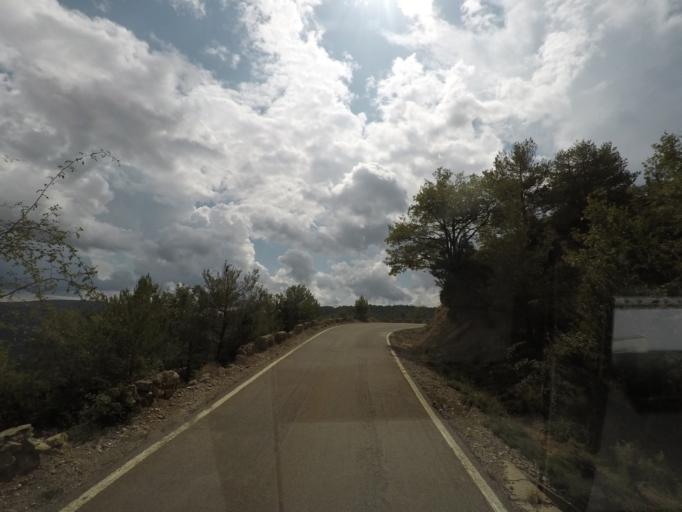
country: ES
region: Aragon
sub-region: Provincia de Huesca
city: Boltana
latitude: 42.4035
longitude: -0.0091
